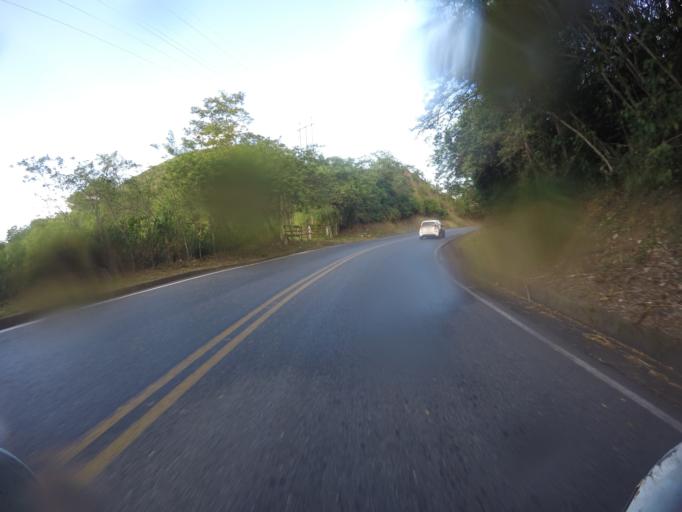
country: CO
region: Valle del Cauca
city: Cartago
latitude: 4.7286
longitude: -75.8631
